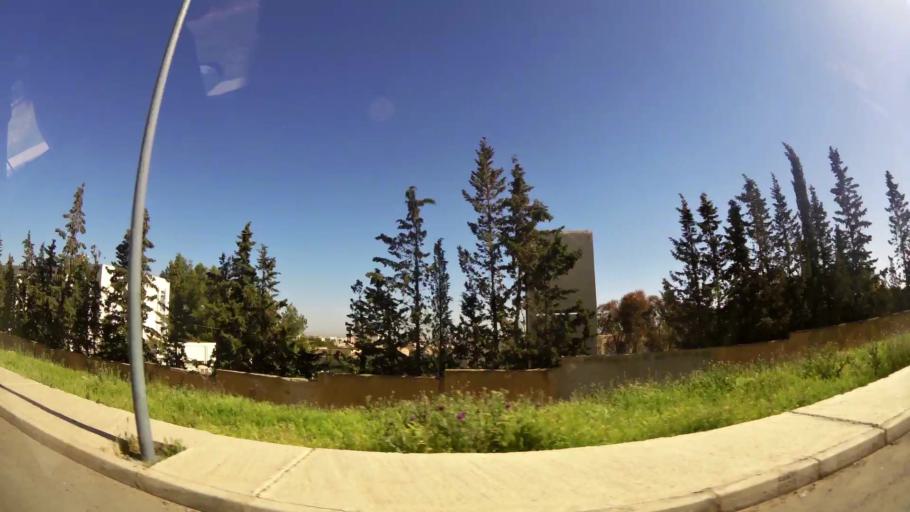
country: MA
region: Oriental
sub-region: Oujda-Angad
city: Oujda
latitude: 34.6479
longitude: -1.8951
